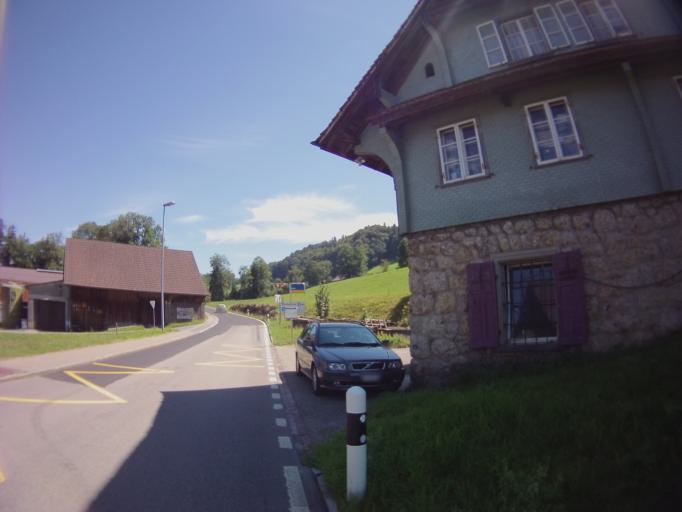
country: CH
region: Schwyz
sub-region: Bezirk Hoefe
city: Feusisberg
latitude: 47.1881
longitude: 8.7604
